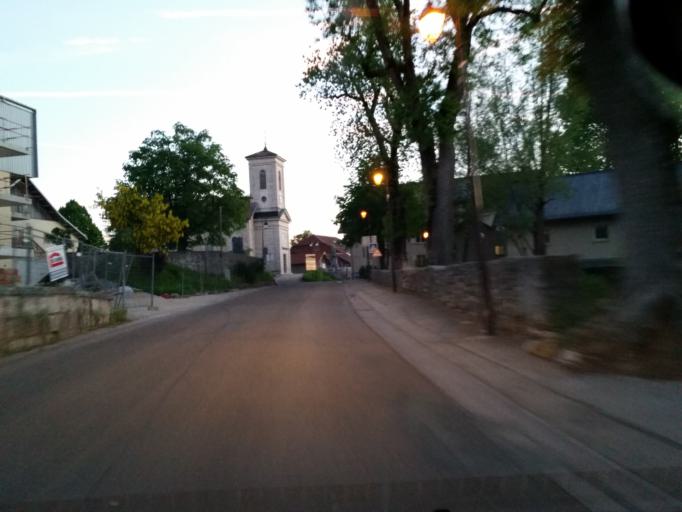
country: FR
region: Franche-Comte
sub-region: Departement du Doubs
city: Jougne
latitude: 46.7742
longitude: 6.3527
